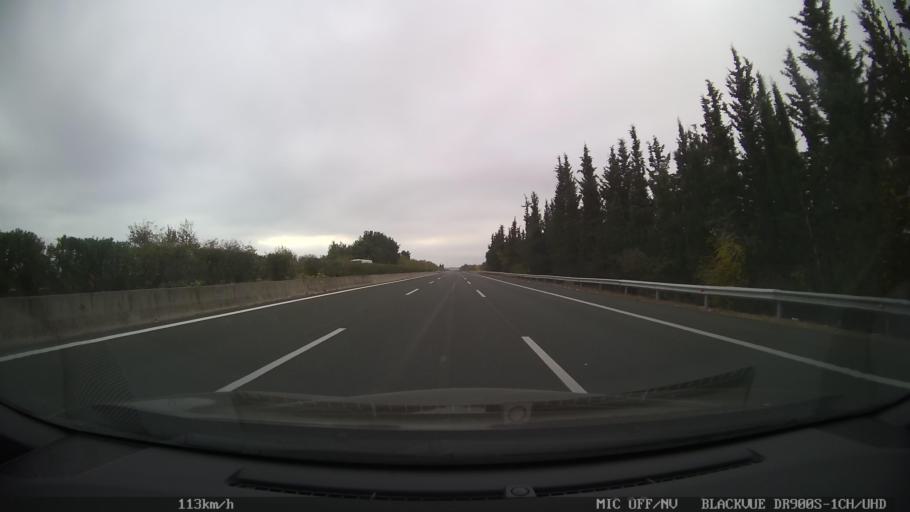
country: GR
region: Central Macedonia
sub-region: Nomos Pierias
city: Aiginio
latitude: 40.4857
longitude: 22.5664
